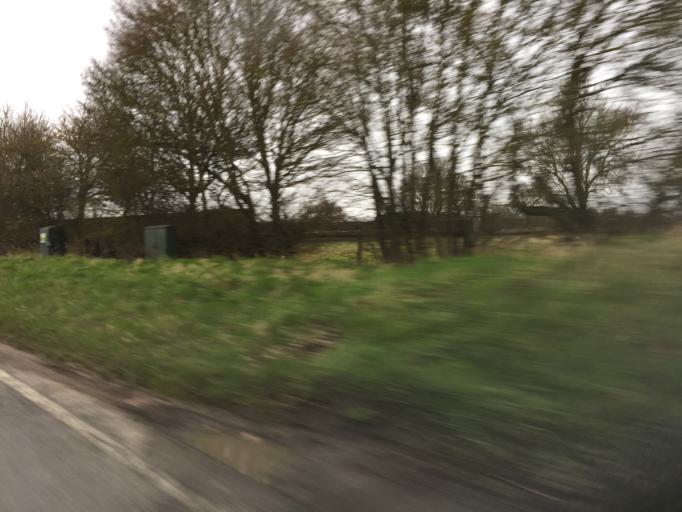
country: GB
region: England
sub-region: Oxfordshire
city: Stanford in the Vale
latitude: 51.6194
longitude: -1.4957
